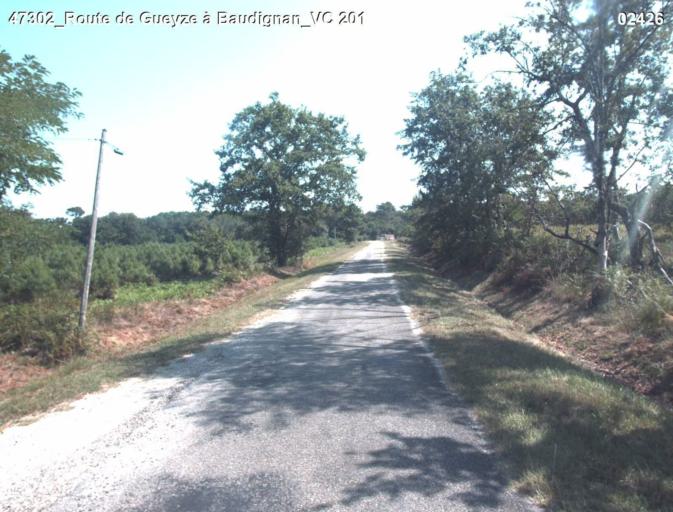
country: FR
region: Aquitaine
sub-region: Departement des Landes
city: Gabarret
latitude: 44.0586
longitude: 0.1108
